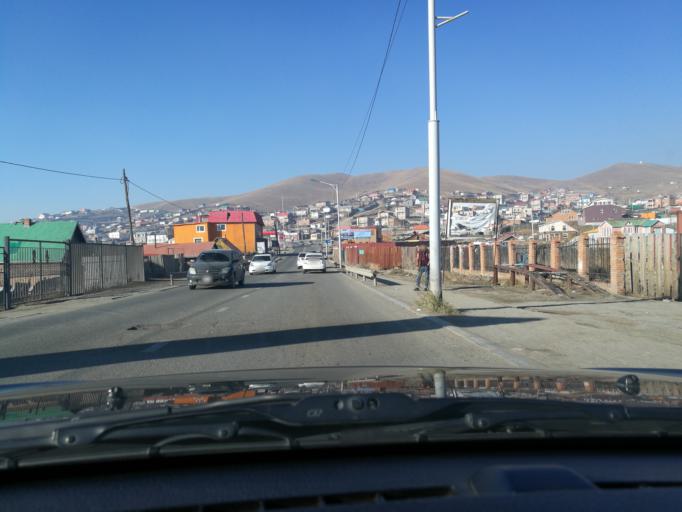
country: MN
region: Ulaanbaatar
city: Ulaanbaatar
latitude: 47.9764
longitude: 106.9220
